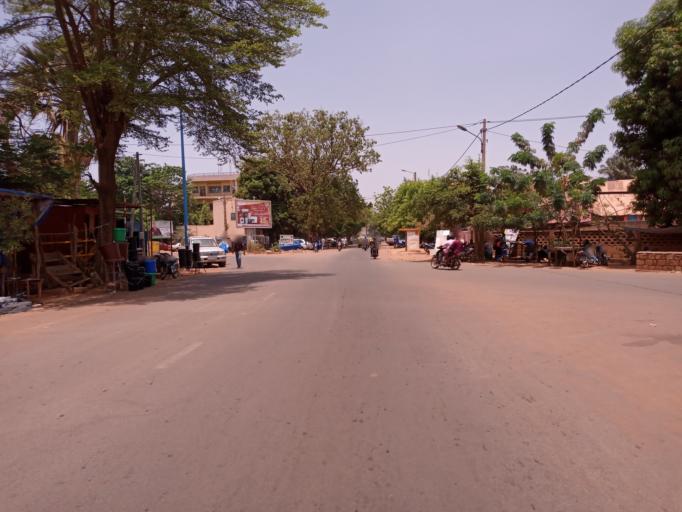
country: ML
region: Bamako
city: Bamako
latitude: 12.6342
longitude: -8.0002
